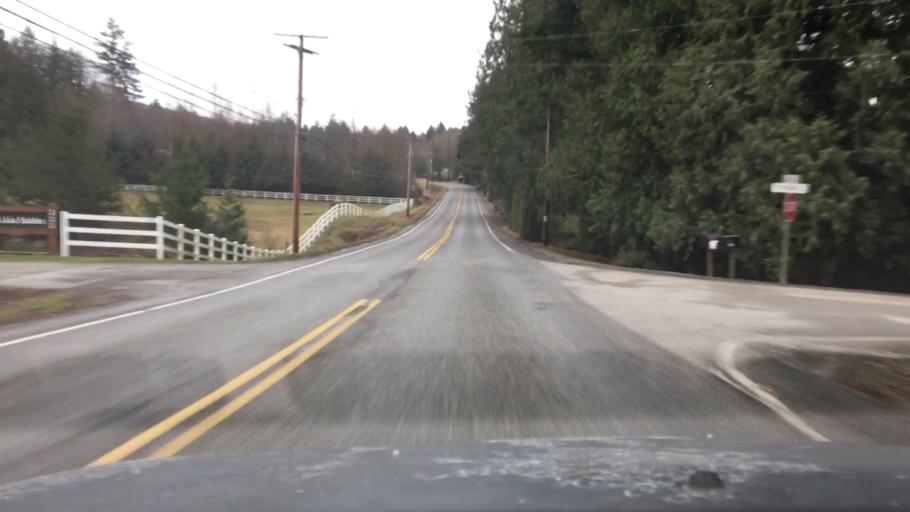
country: US
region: Washington
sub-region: Whatcom County
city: Sudden Valley
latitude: 48.6495
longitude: -122.3243
